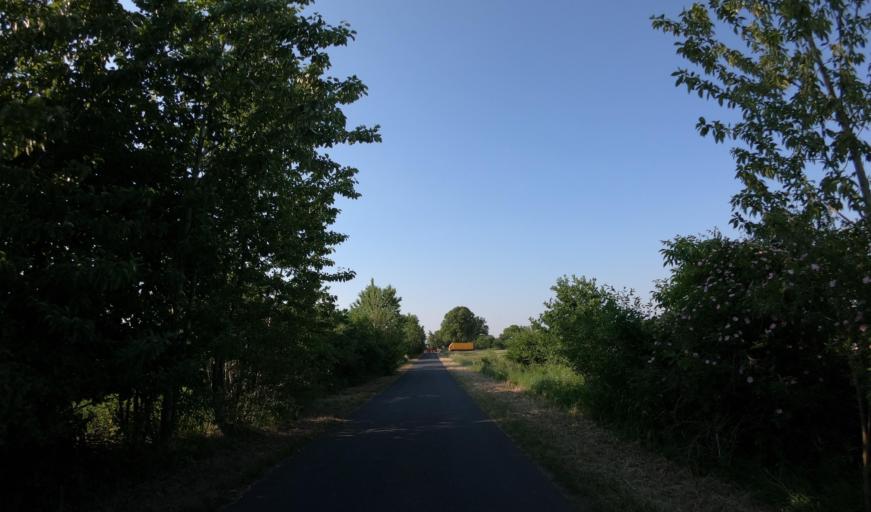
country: PL
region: West Pomeranian Voivodeship
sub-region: Powiat lobeski
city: Radowo Male
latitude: 53.6540
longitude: 15.4116
